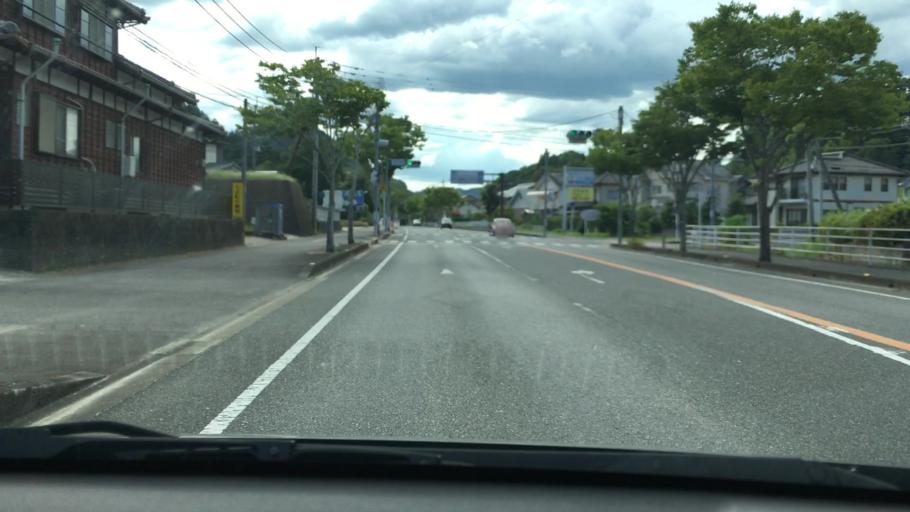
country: JP
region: Saga Prefecture
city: Takeocho-takeo
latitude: 33.1868
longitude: 130.0331
